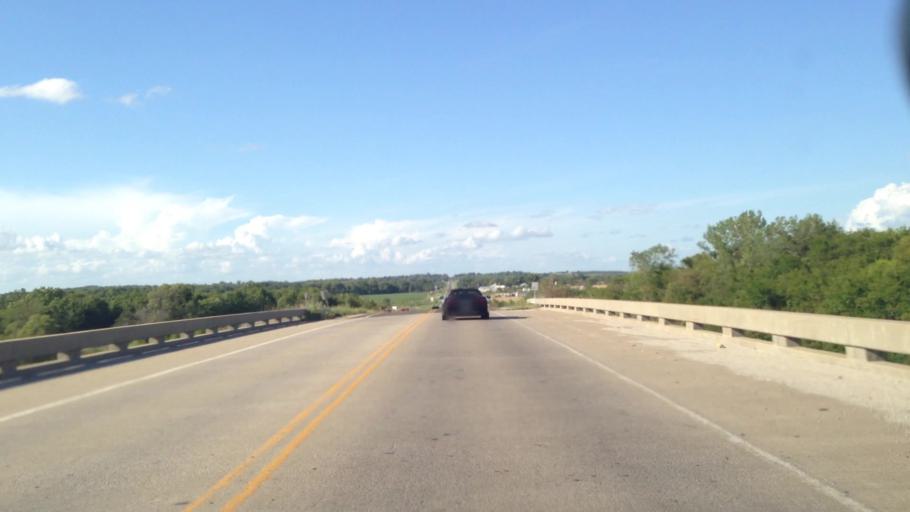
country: US
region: Kansas
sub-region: Franklin County
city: Ottawa
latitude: 38.6353
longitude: -95.2677
